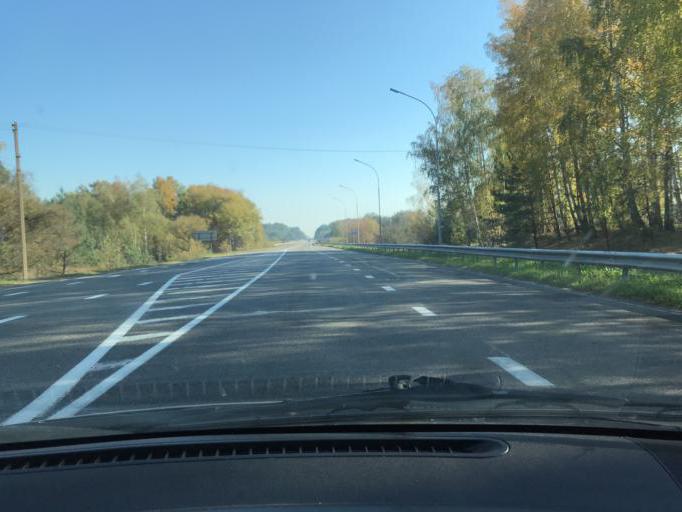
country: BY
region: Brest
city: Davyd-Haradok
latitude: 52.2477
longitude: 27.0850
